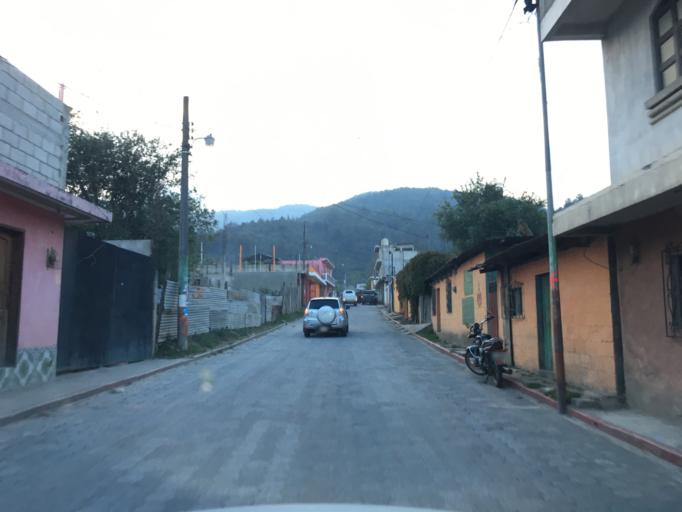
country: GT
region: Chimaltenango
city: Tecpan Guatemala
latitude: 14.7574
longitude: -91.0002
